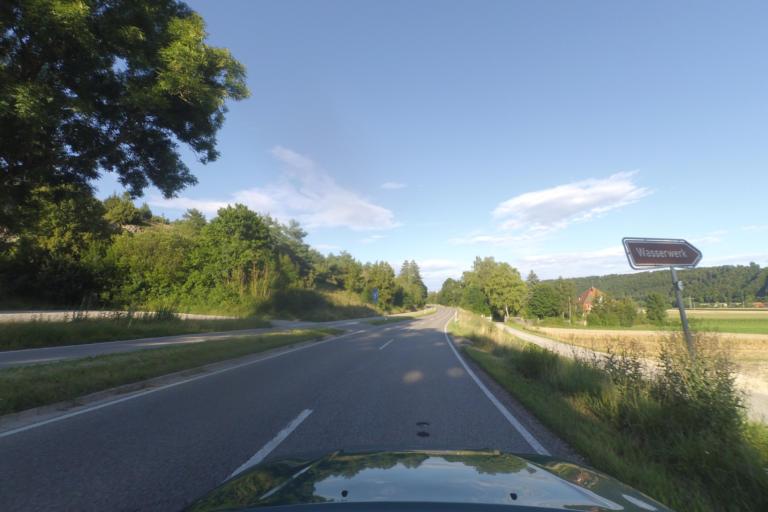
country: DE
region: Bavaria
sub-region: Upper Bavaria
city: Eichstaett
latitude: 48.8811
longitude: 11.2244
